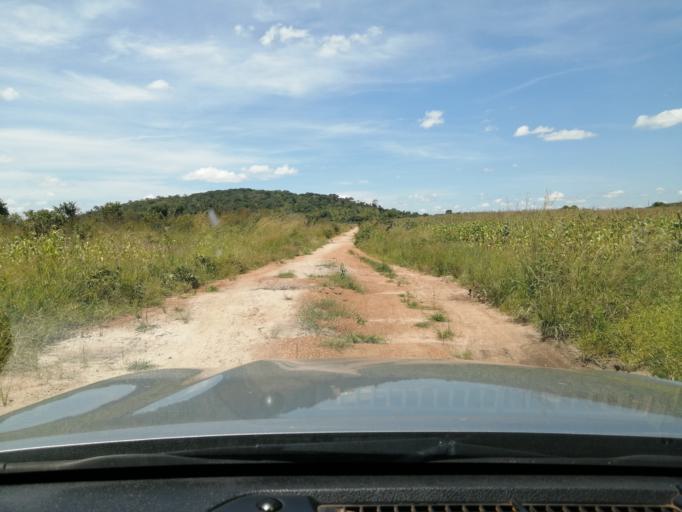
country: ZM
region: Central
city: Chibombo
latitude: -15.0948
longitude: 27.8415
